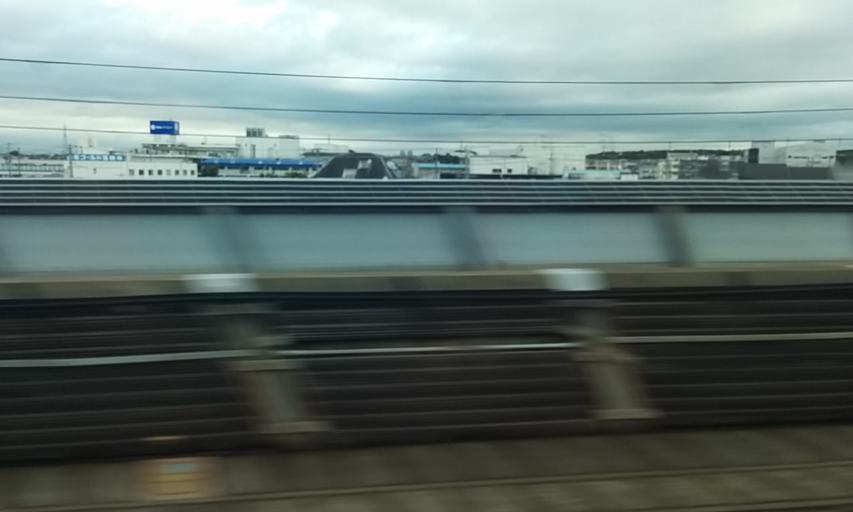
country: JP
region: Hyogo
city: Akashi
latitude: 34.6647
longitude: 134.9962
